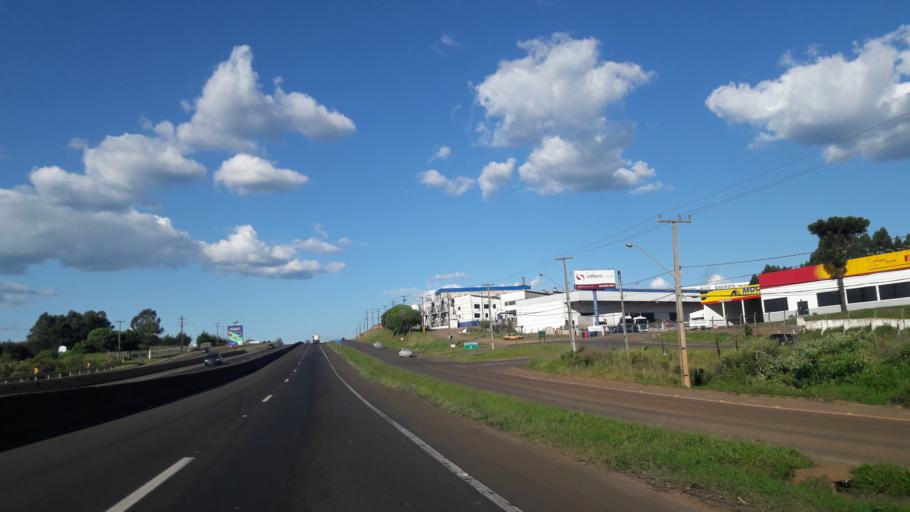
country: BR
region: Parana
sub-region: Guarapuava
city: Guarapuava
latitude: -25.3566
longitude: -51.4626
